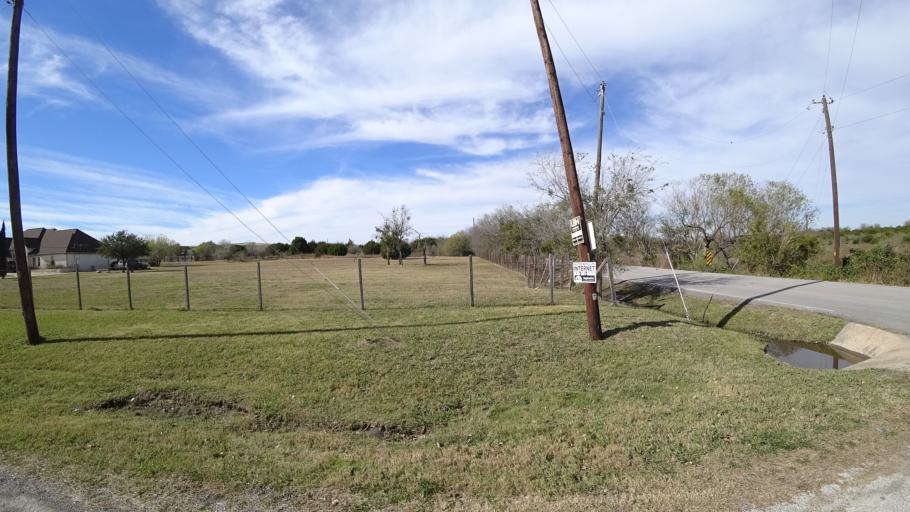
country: US
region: Texas
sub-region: Travis County
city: Onion Creek
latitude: 30.1104
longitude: -97.7472
